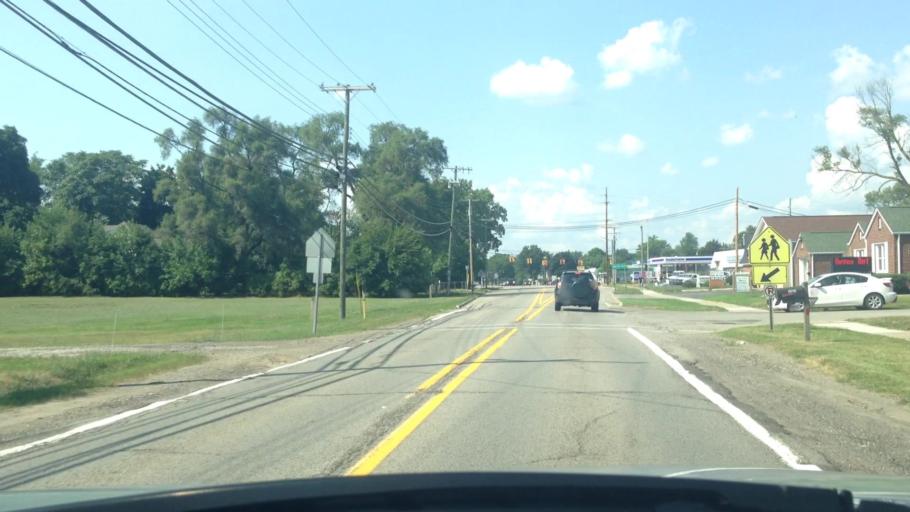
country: US
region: Michigan
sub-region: Oakland County
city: Waterford
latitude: 42.6878
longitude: -83.3731
